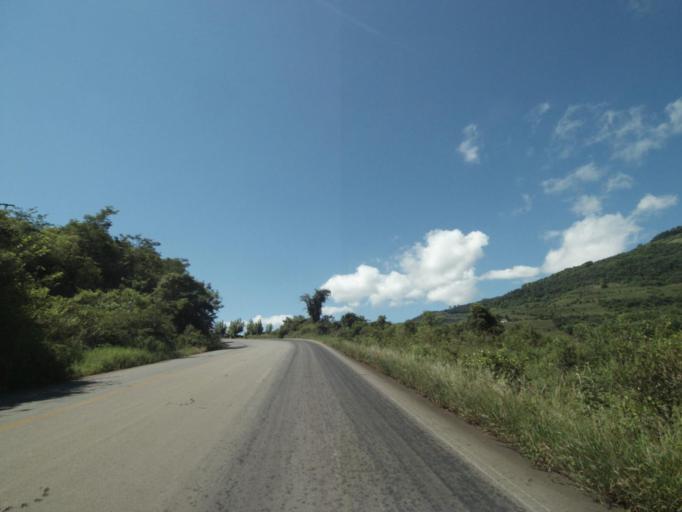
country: BR
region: Rio Grande do Sul
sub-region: Bento Goncalves
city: Bento Goncalves
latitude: -29.0993
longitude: -51.6266
